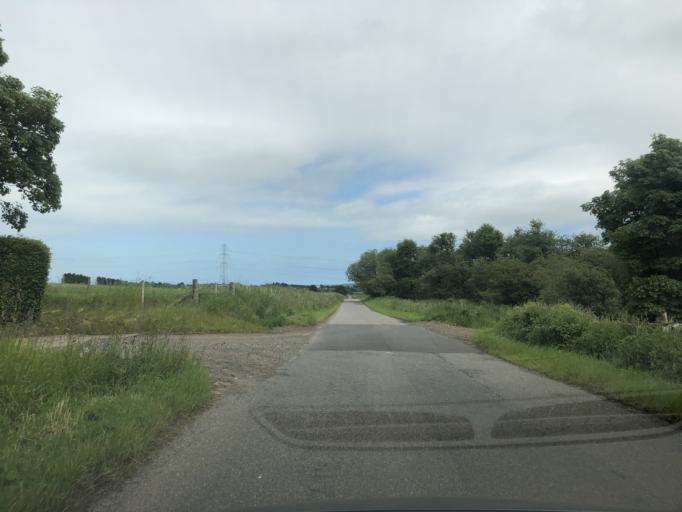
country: GB
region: Scotland
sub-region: Angus
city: Brechin
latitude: 56.7368
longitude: -2.7042
